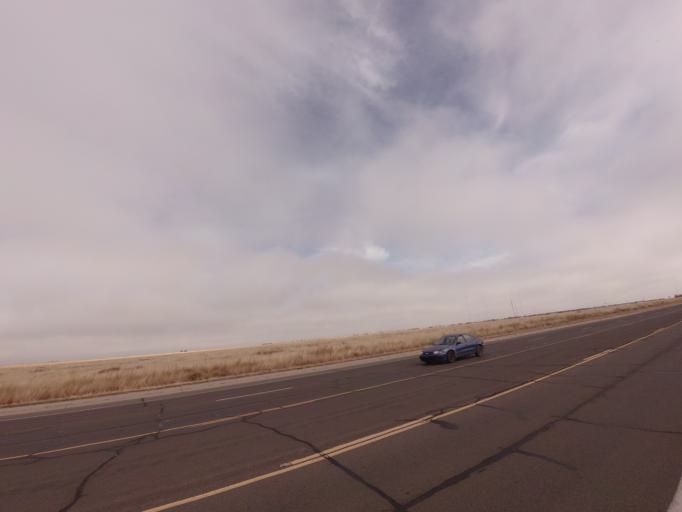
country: US
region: New Mexico
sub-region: Curry County
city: Clovis
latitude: 34.4340
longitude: -103.2240
